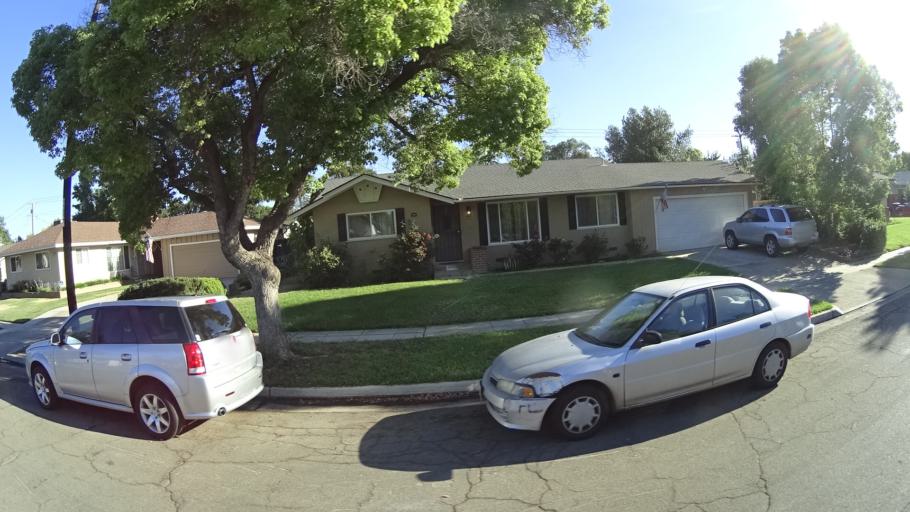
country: US
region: California
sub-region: Fresno County
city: Fresno
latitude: 36.8003
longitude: -119.8233
